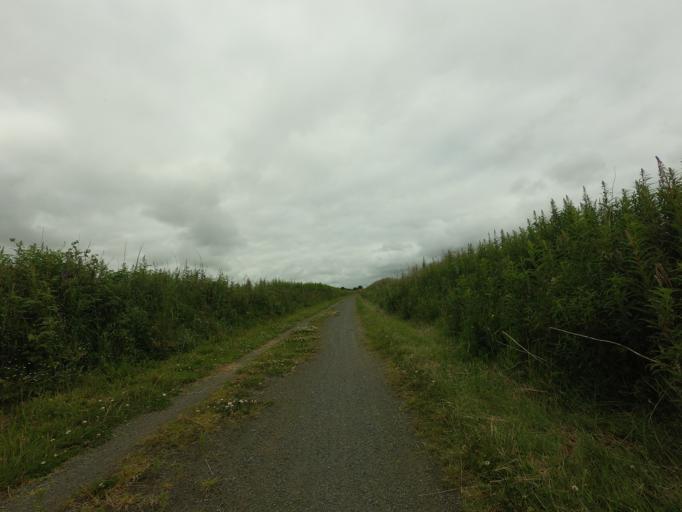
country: GB
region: Scotland
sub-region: Aberdeenshire
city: Ellon
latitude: 57.4831
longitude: -2.1346
